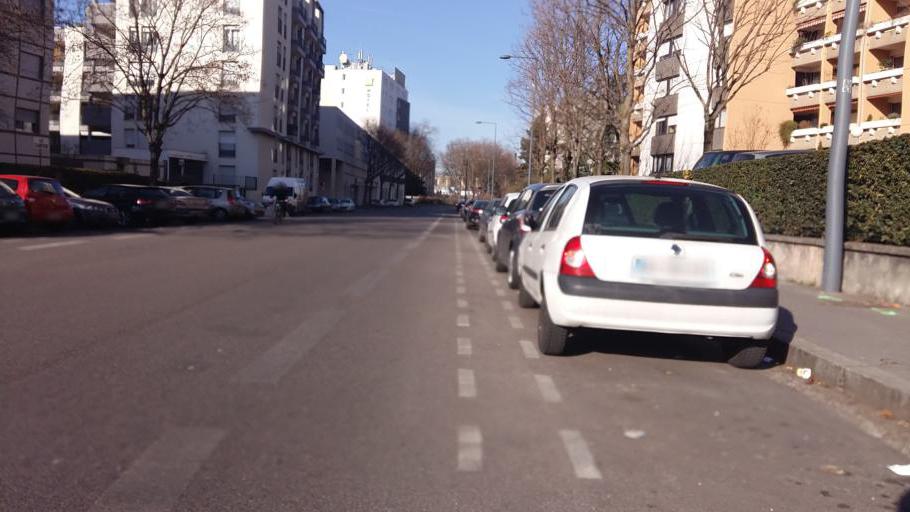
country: FR
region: Rhone-Alpes
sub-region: Departement du Rhone
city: Villeurbanne
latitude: 45.7777
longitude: 4.8744
